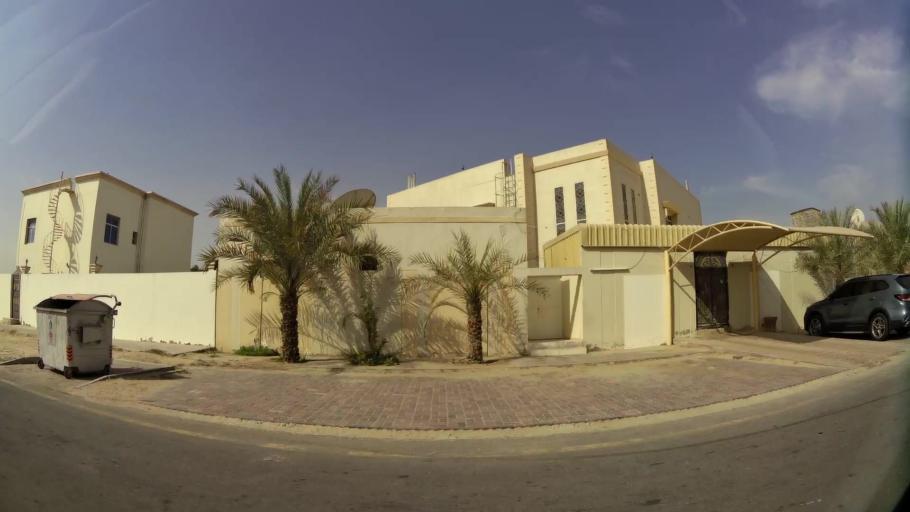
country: AE
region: Ash Shariqah
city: Sharjah
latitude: 25.2656
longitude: 55.3951
